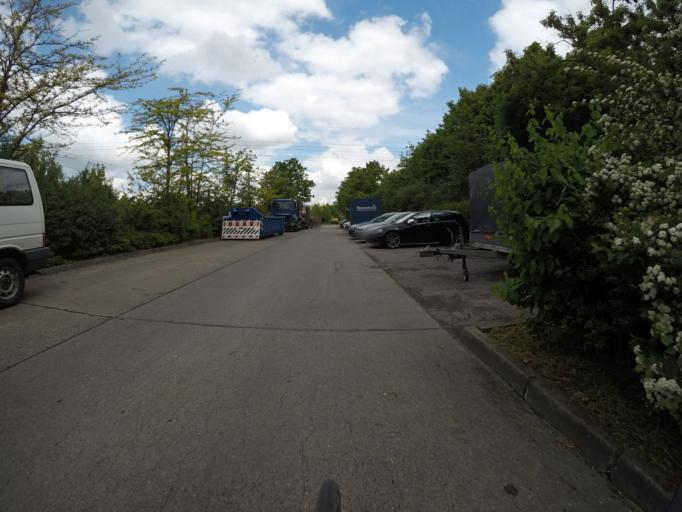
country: DE
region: Berlin
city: Marzahn
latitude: 52.5600
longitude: 13.5694
